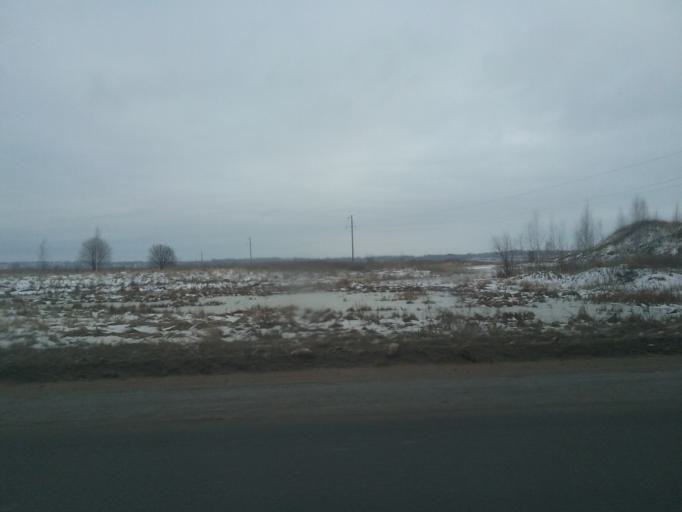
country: RU
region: Tula
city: Bolokhovo
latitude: 54.0609
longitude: 37.8032
